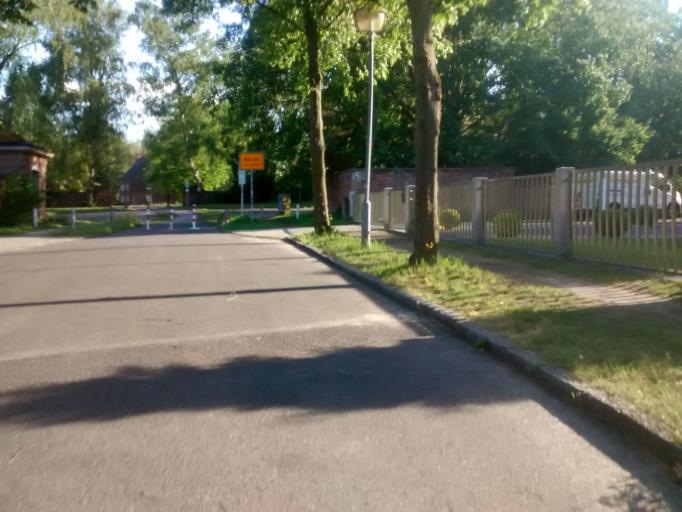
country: DE
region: Brandenburg
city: Hohen Neuendorf
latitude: 52.6606
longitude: 13.2847
